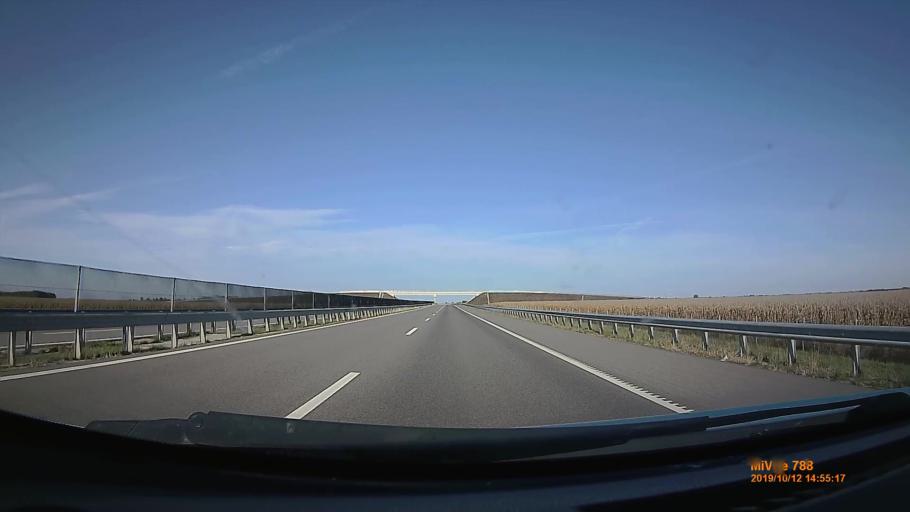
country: HU
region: Hajdu-Bihar
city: Derecske
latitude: 47.4019
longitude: 21.5444
